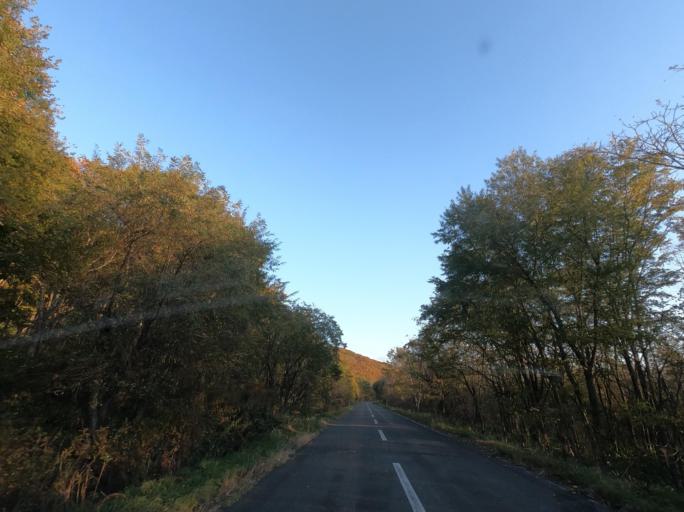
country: JP
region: Hokkaido
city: Kushiro
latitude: 43.2164
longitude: 144.4511
